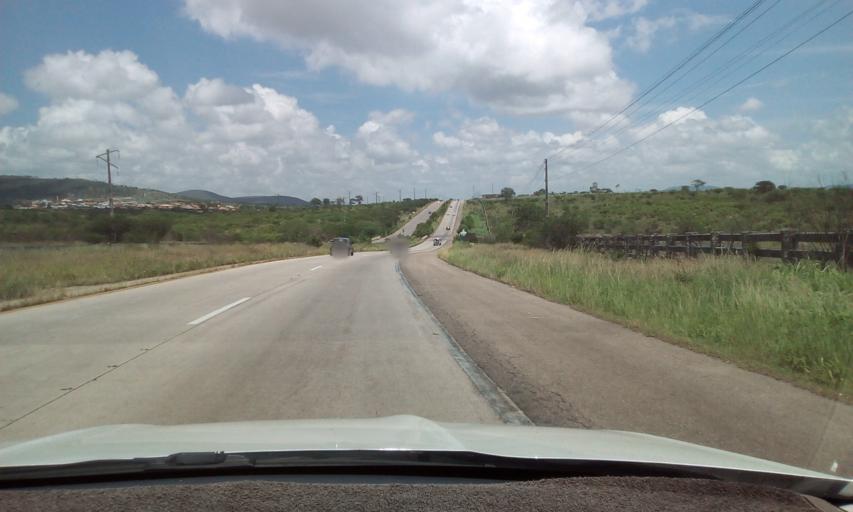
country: BR
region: Pernambuco
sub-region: Gravata
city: Gravata
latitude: -8.2142
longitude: -35.6304
